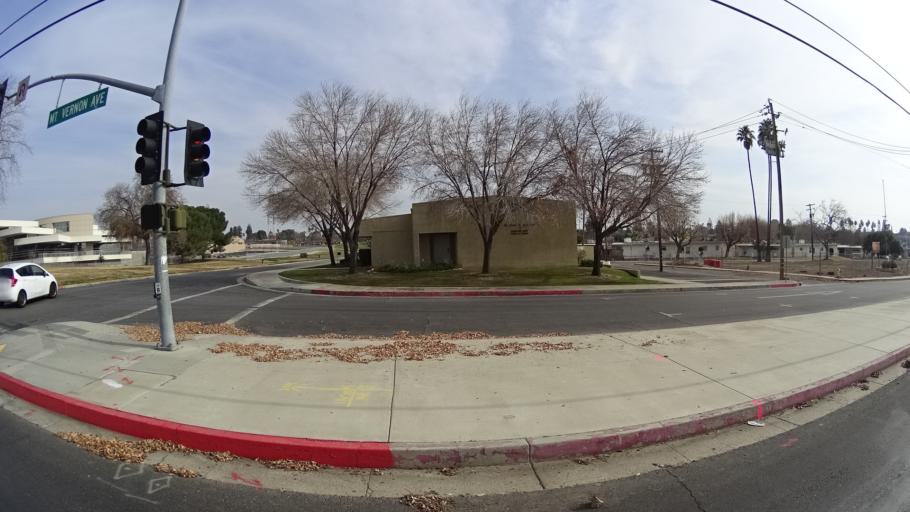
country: US
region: California
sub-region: Kern County
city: Oildale
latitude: 35.4104
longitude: -118.9675
